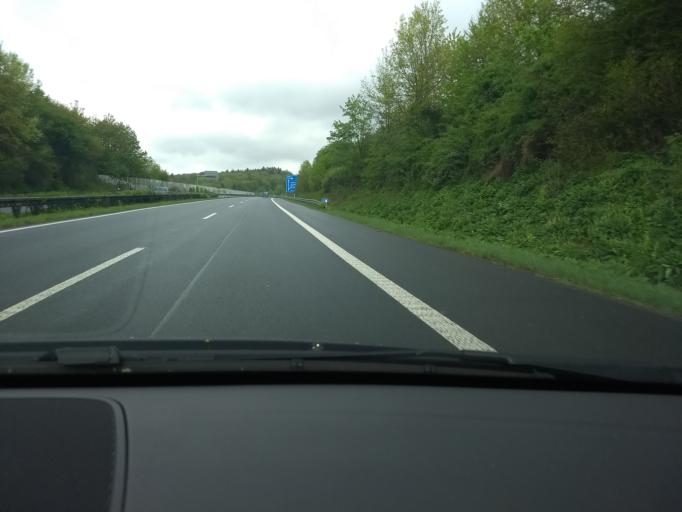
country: DE
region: North Rhine-Westphalia
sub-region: Regierungsbezirk Arnsberg
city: Arnsberg
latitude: 51.4138
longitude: 8.0704
